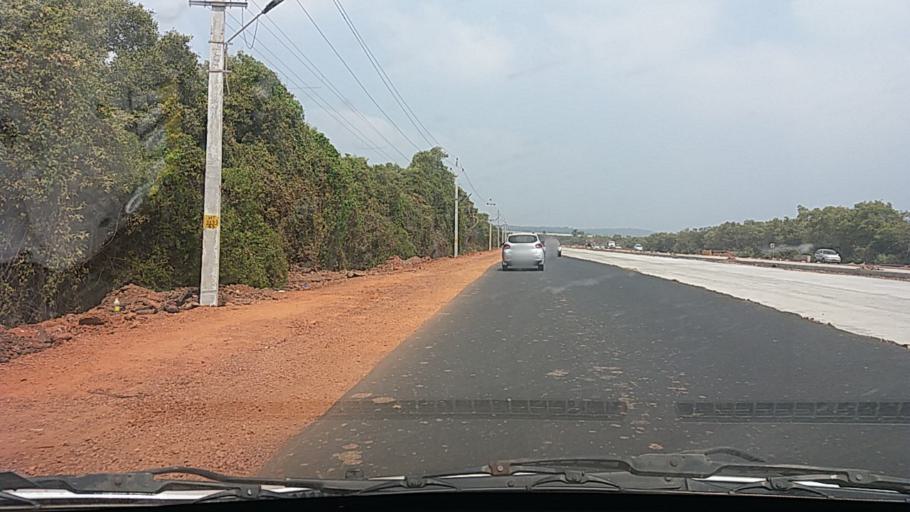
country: IN
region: Goa
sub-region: North Goa
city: Taleigao
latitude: 15.4860
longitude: 73.8463
